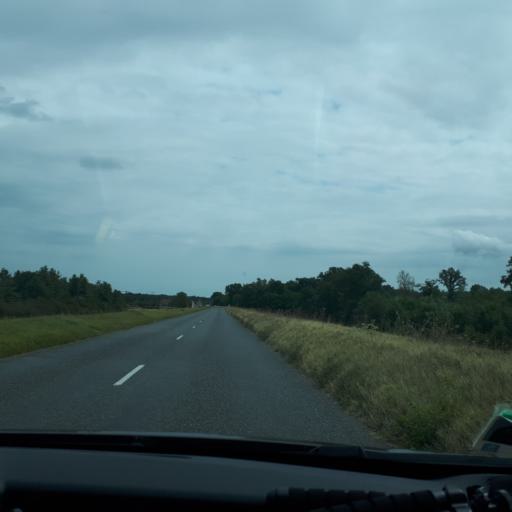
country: FR
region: Centre
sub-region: Departement du Loiret
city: Sully-sur-Loire
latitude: 47.7718
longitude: 2.4175
